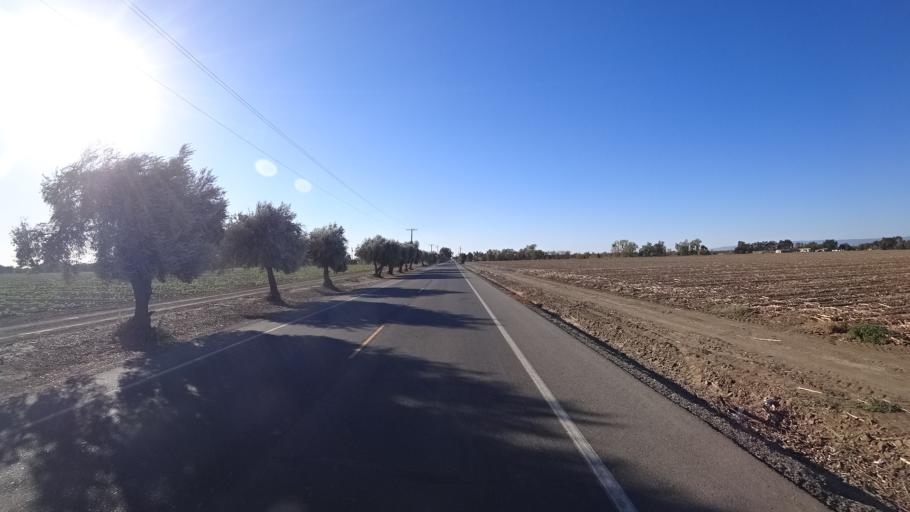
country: US
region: California
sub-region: Yolo County
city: Woodland
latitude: 38.6103
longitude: -121.7853
